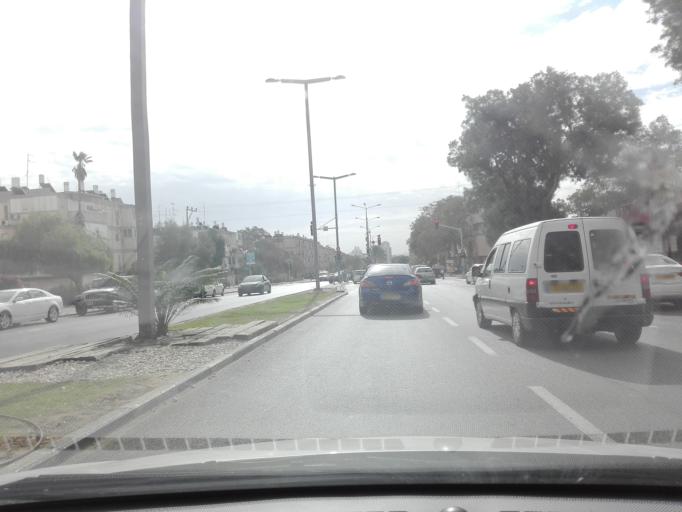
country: IL
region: Southern District
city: Beersheba
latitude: 31.2703
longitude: 34.7980
